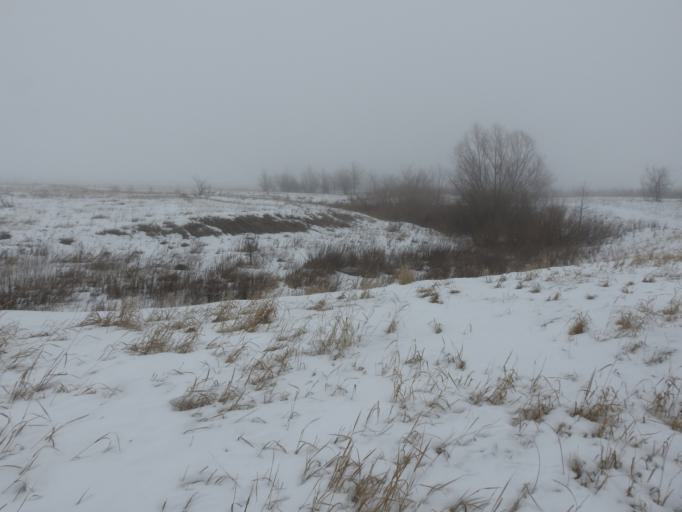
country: RU
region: Saratov
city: Sokolovyy
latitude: 51.4958
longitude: 45.8367
